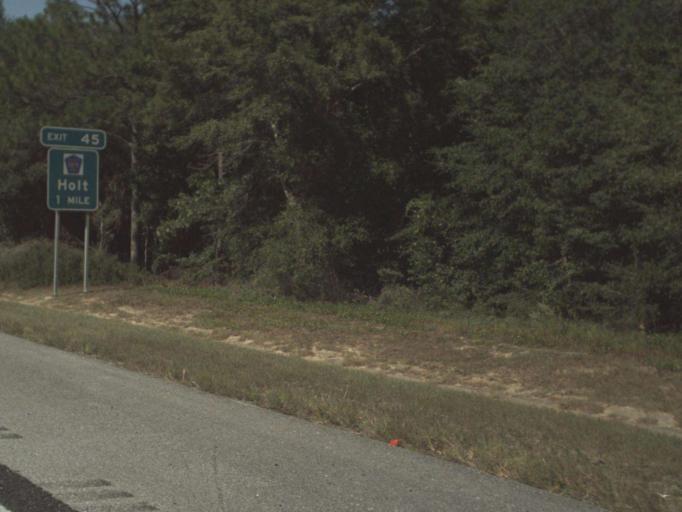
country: US
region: Florida
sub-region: Okaloosa County
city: Crestview
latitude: 30.7063
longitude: -86.7318
